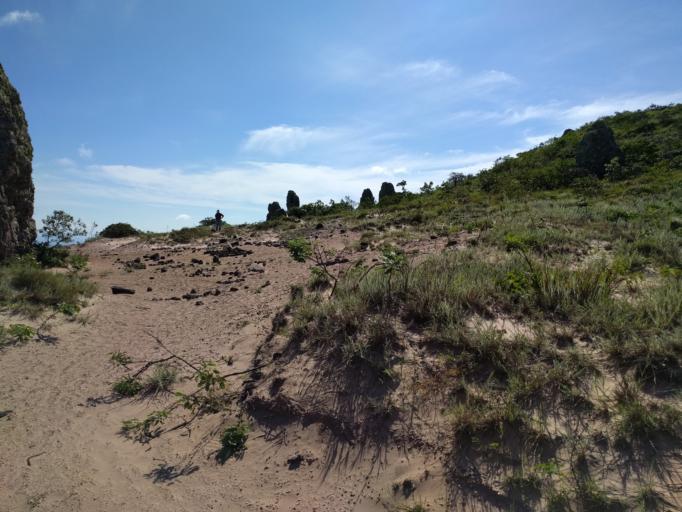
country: BO
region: Santa Cruz
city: Robore
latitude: -18.3230
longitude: -59.5714
